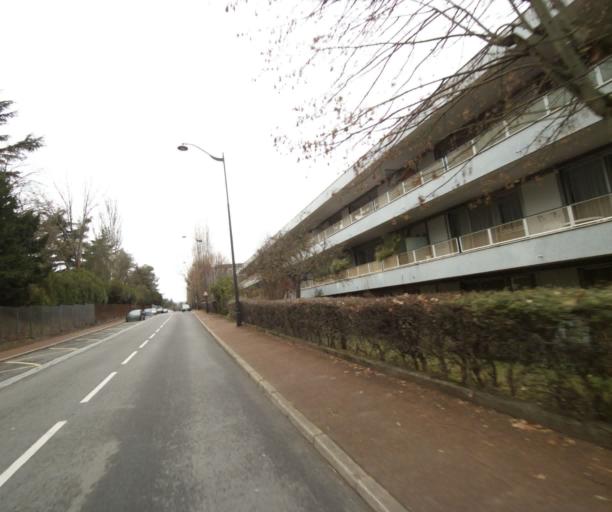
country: FR
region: Ile-de-France
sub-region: Departement des Hauts-de-Seine
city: Garches
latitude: 48.8596
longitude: 2.1815
